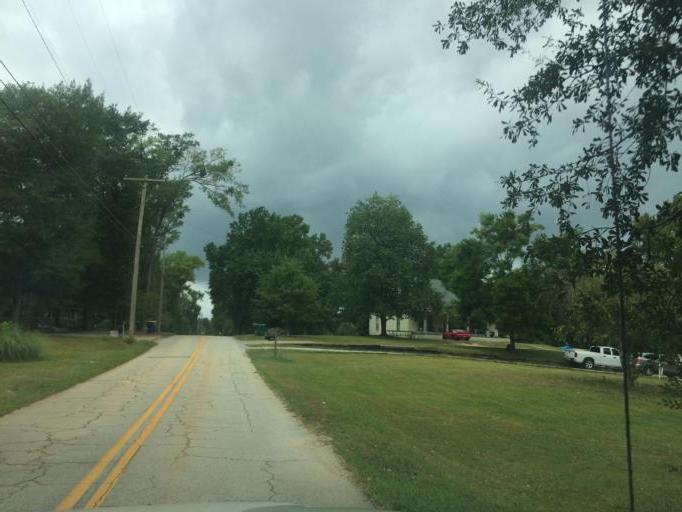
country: US
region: Georgia
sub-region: Elbert County
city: Elberton
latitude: 34.1286
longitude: -82.8610
